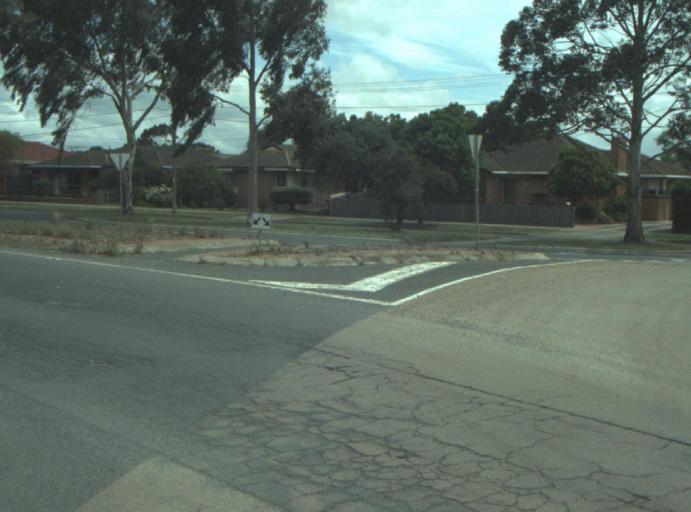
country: AU
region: Victoria
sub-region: Greater Geelong
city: Bell Park
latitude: -38.0667
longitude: 144.3589
